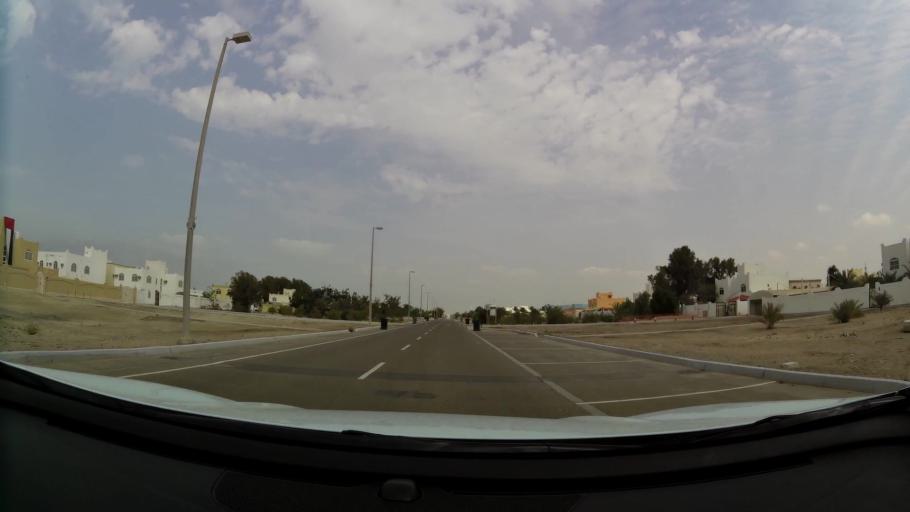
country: AE
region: Abu Dhabi
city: Abu Dhabi
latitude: 24.5405
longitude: 54.6298
